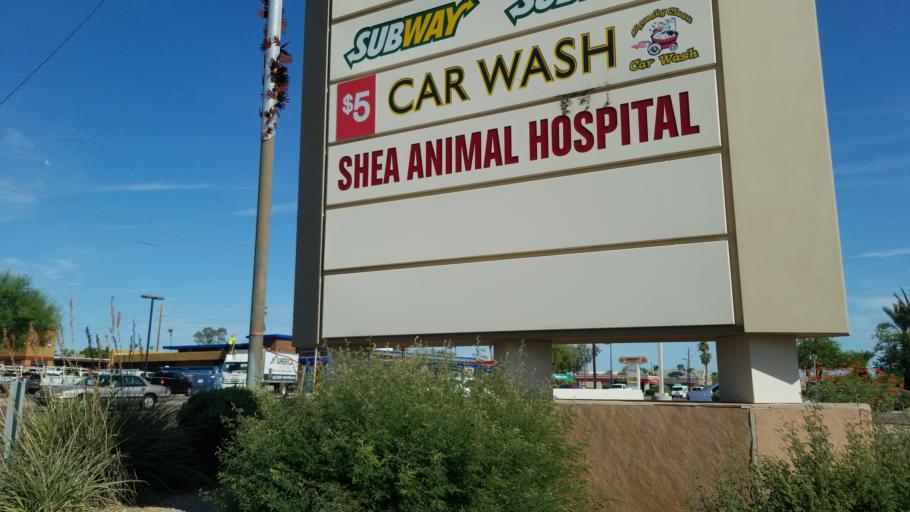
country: US
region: Arizona
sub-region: Maricopa County
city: Paradise Valley
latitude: 33.5853
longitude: -112.0114
